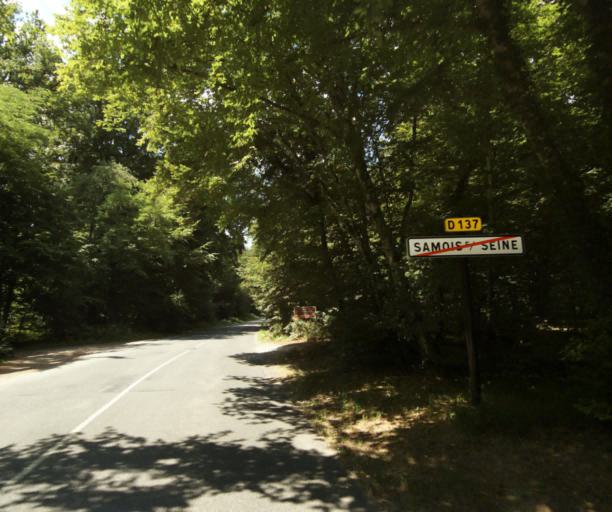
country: FR
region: Ile-de-France
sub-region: Departement de Seine-et-Marne
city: Samois-sur-Seine
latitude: 48.4534
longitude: 2.7373
